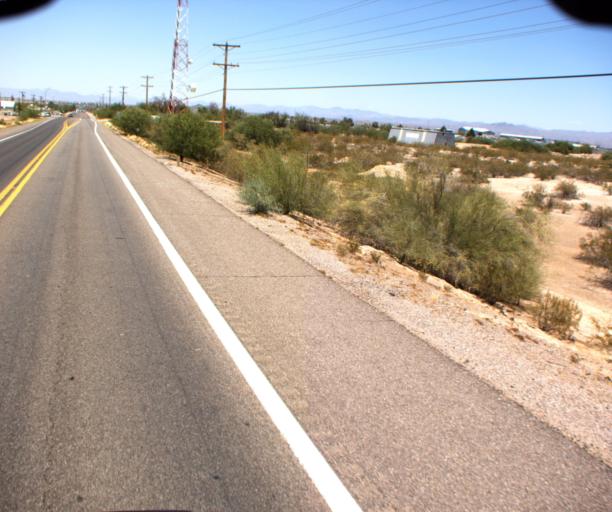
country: US
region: Arizona
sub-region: Pinal County
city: Florence
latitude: 33.0204
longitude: -111.3791
